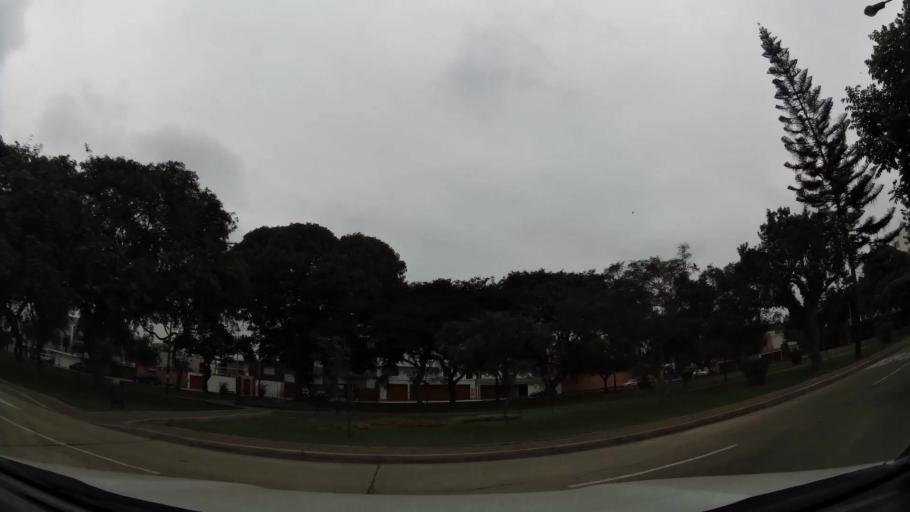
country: PE
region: Lima
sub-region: Lima
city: San Luis
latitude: -12.0958
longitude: -77.0146
